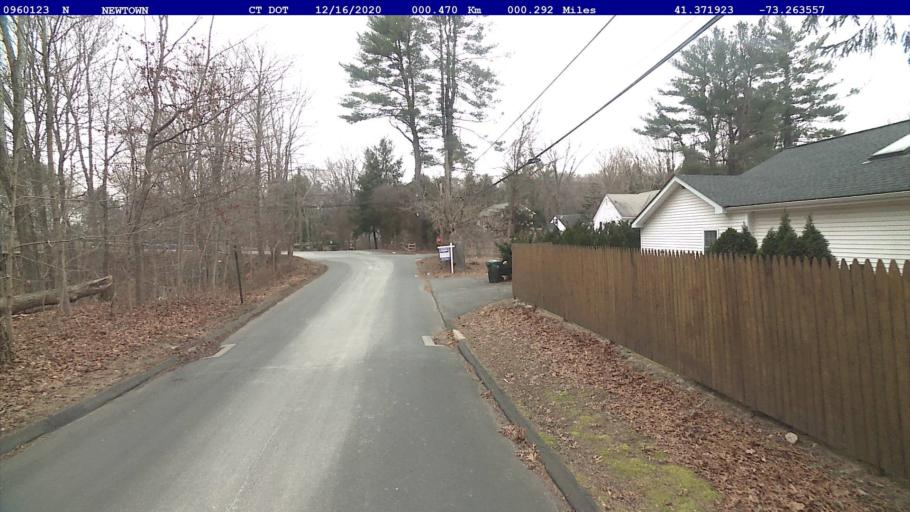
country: US
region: Connecticut
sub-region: Fairfield County
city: Newtown
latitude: 41.3719
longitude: -73.2636
